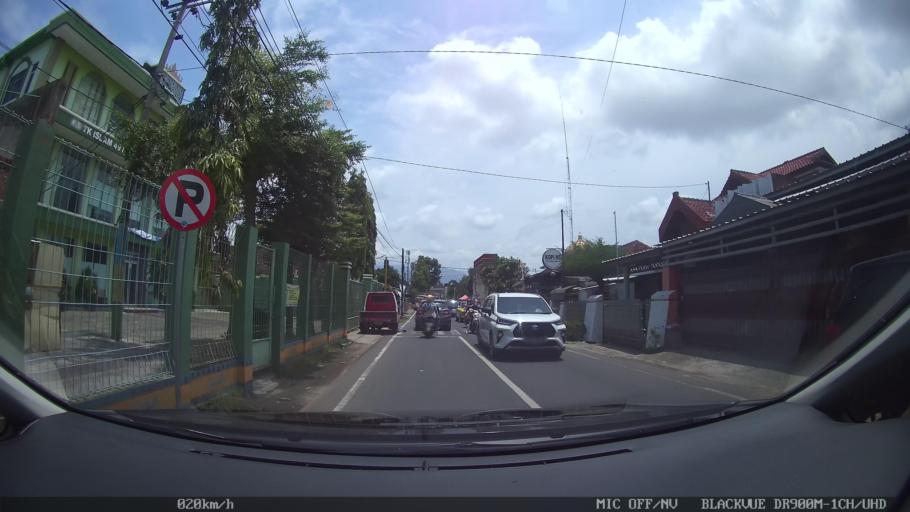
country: ID
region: Lampung
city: Kedaton
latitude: -5.3847
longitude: 105.2576
